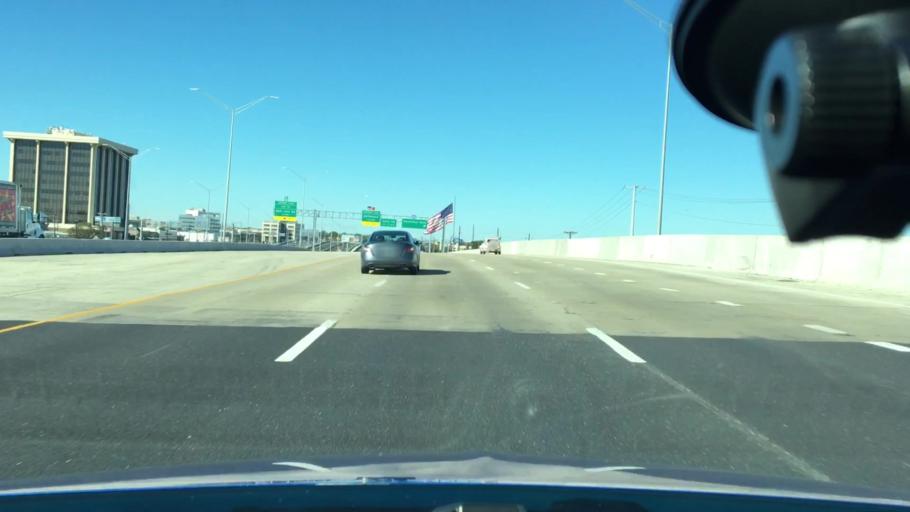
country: US
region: Texas
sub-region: Dallas County
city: Irving
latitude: 32.8375
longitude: -96.9507
